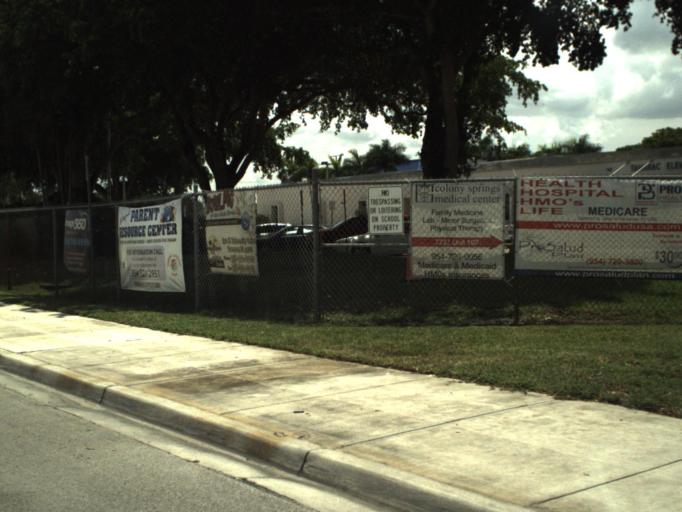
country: US
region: Florida
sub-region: Broward County
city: Tamarac
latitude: 26.2170
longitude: -80.2527
